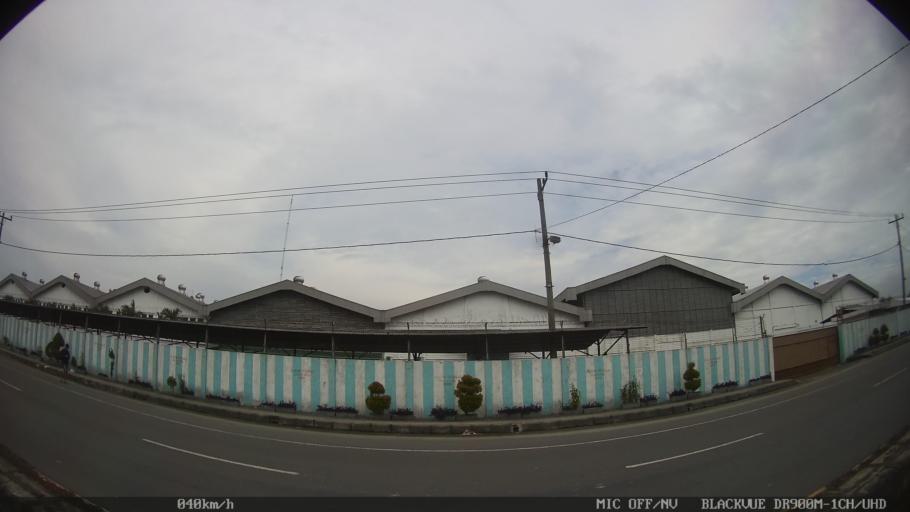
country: ID
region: North Sumatra
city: Sunggal
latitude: 3.6039
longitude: 98.5752
